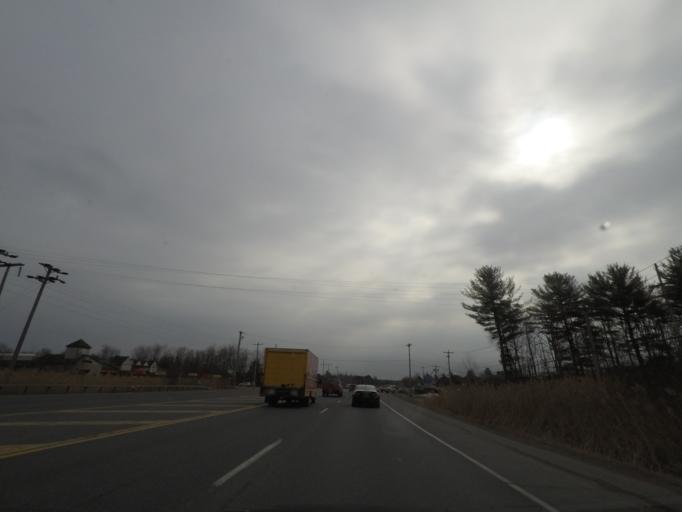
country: US
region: New York
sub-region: Warren County
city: Glens Falls
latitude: 43.3322
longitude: -73.6505
